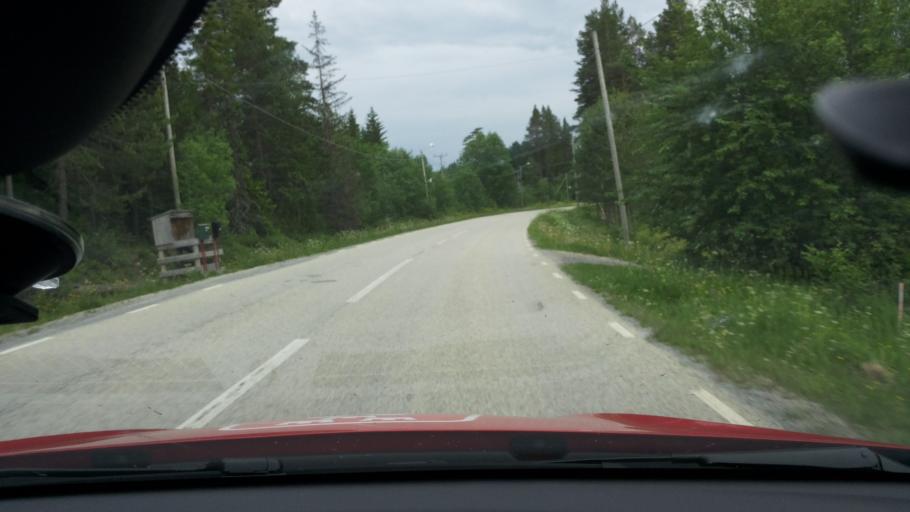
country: SE
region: Jaemtland
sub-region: Bergs Kommun
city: Hoverberg
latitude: 62.6767
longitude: 14.2944
